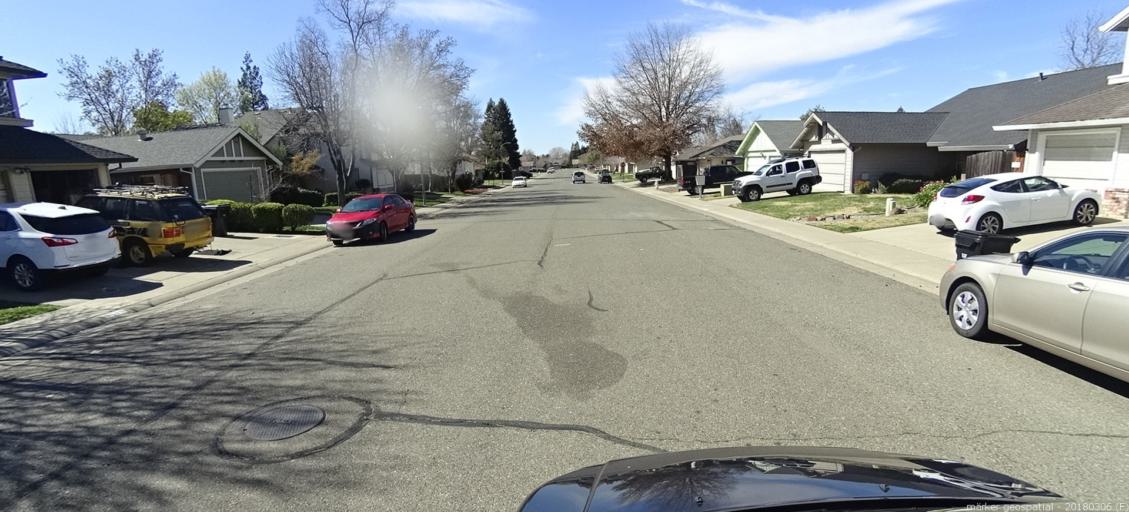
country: US
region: California
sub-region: Sacramento County
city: Vineyard
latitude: 38.4671
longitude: -121.3609
